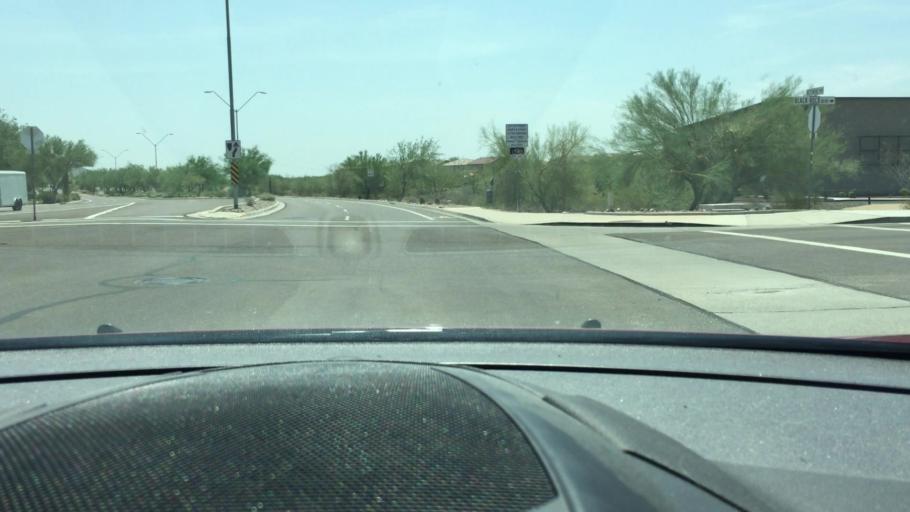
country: US
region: Arizona
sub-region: Maricopa County
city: Sun City West
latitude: 33.7301
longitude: -112.2521
